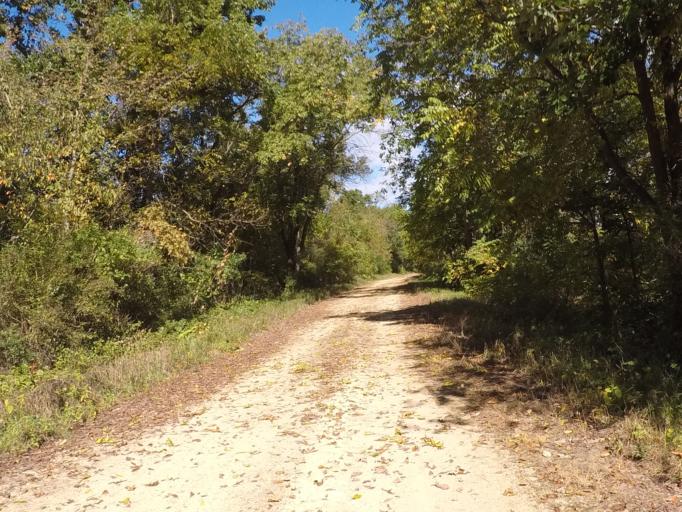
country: US
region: Wisconsin
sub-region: Richland County
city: Richland Center
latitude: 43.2251
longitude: -90.2975
